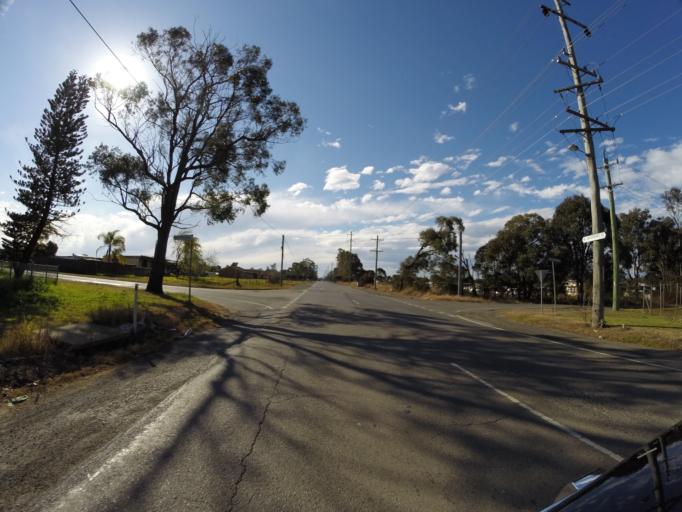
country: AU
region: New South Wales
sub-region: Fairfield
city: Cecil Park
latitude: -33.8939
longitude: 150.7902
